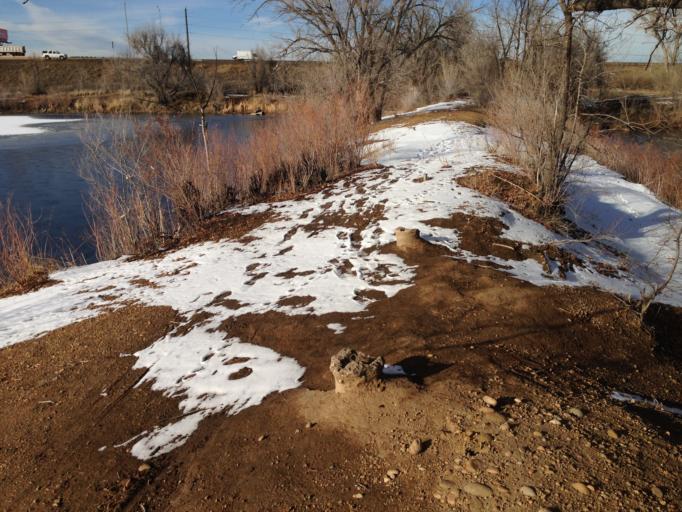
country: US
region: Colorado
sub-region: Adams County
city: Berkley
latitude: 39.7975
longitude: -105.0417
